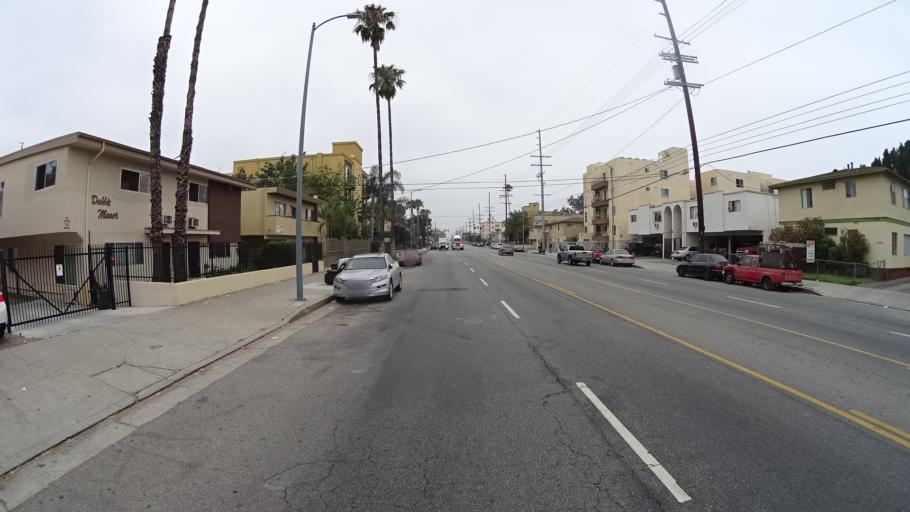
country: US
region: California
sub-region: Los Angeles County
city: Van Nuys
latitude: 34.1939
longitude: -118.4249
